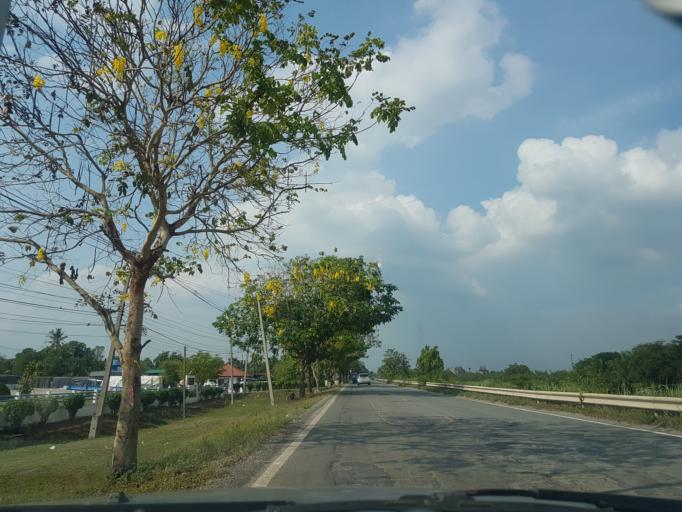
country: TH
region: Phra Nakhon Si Ayutthaya
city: Phachi
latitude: 14.4106
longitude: 100.7844
